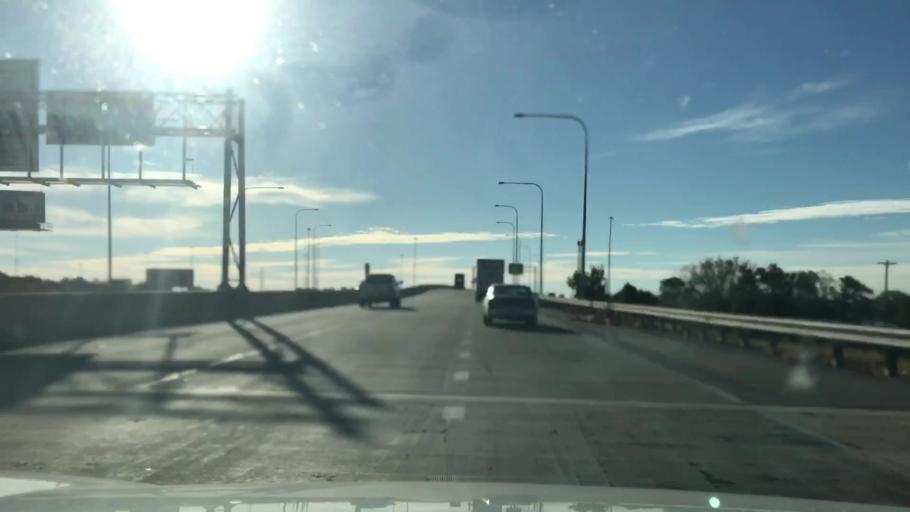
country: US
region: Illinois
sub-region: Saint Clair County
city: East Saint Louis
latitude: 38.6370
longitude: -90.1497
